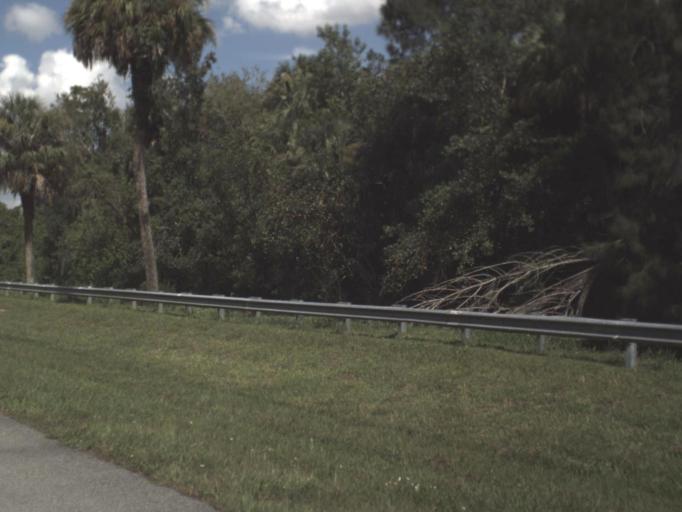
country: US
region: Florida
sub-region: Collier County
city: Immokalee
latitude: 26.2662
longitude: -81.3420
